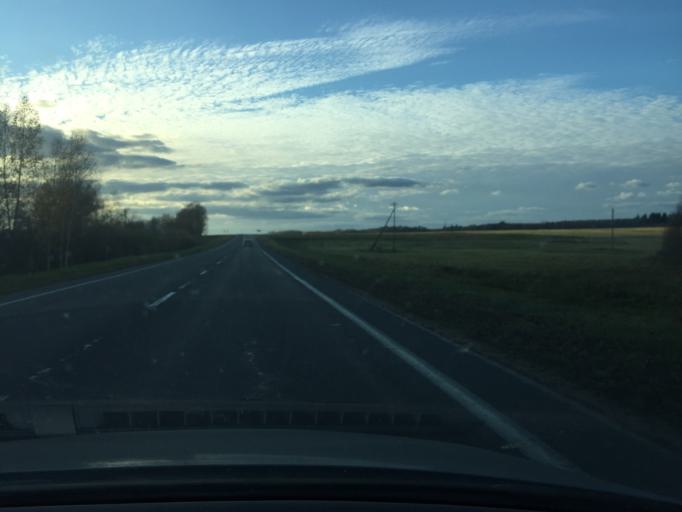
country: BY
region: Vitebsk
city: Vyerkhnyadzvinsk
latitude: 55.8391
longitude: 27.8715
